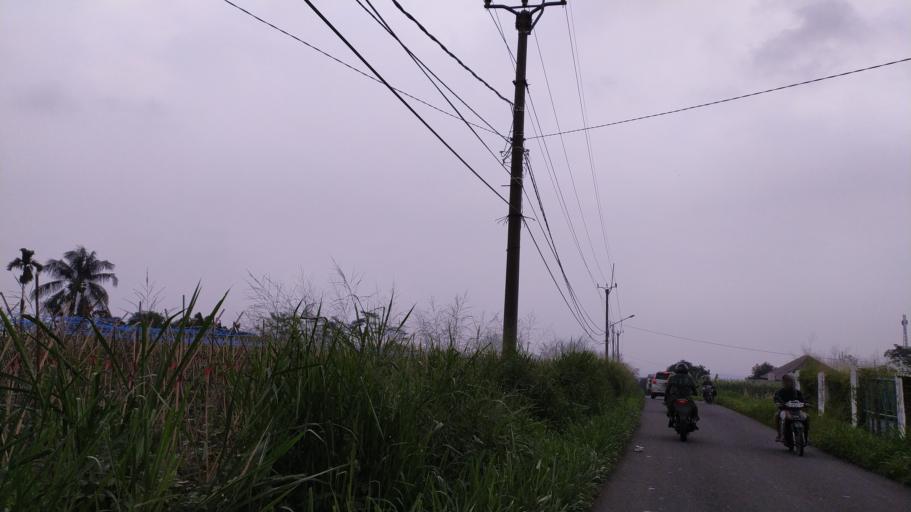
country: ID
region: West Java
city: Ciampea
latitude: -6.6104
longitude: 106.6975
